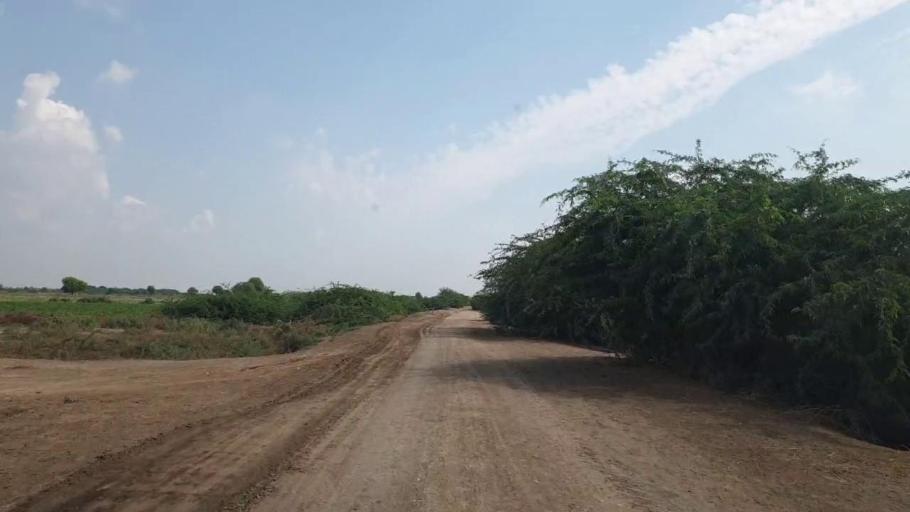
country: PK
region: Sindh
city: Badin
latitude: 24.4774
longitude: 68.6333
